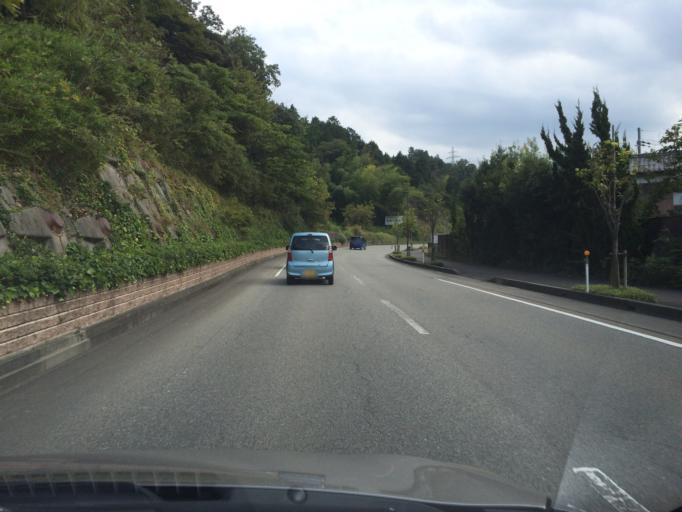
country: JP
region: Hyogo
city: Toyooka
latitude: 35.5306
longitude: 134.8081
